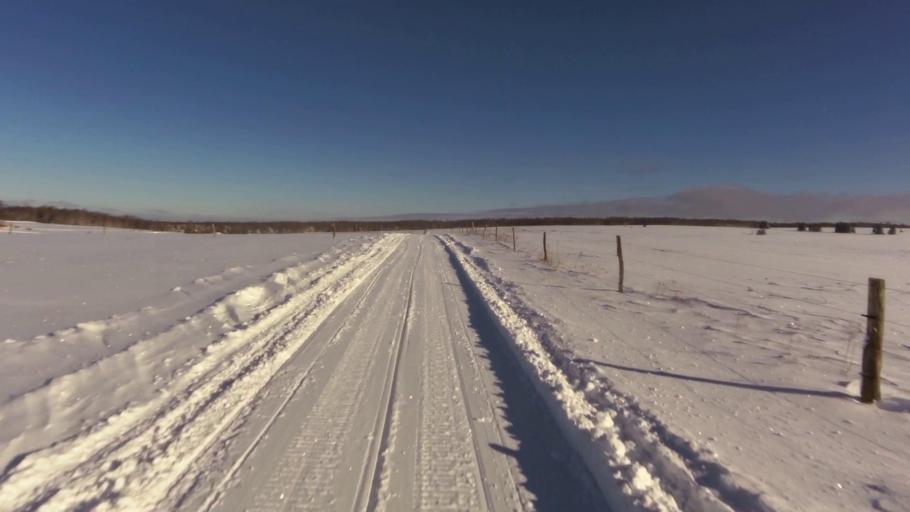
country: US
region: New York
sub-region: Chautauqua County
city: Falconer
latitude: 42.2577
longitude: -79.2029
